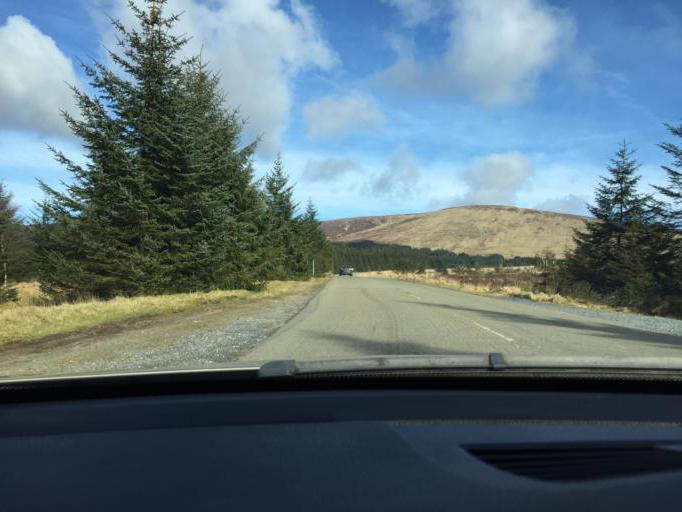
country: IE
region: Leinster
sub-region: Wicklow
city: Valleymount
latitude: 53.0571
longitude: -6.4245
